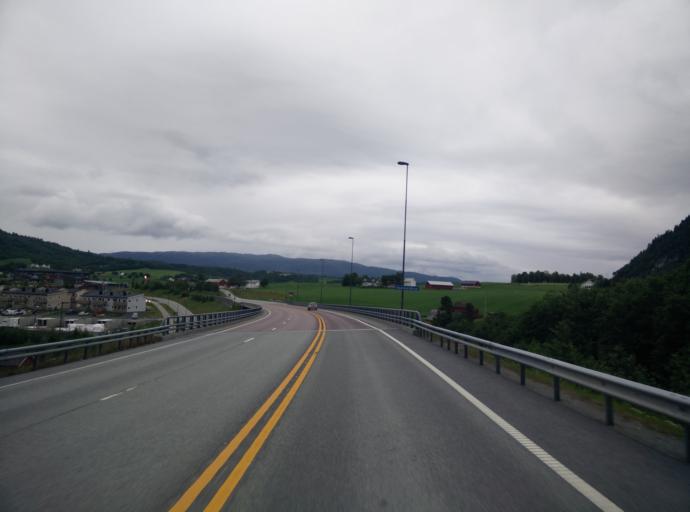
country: NO
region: Sor-Trondelag
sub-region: Skaun
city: Borsa
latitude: 63.3089
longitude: 10.1641
